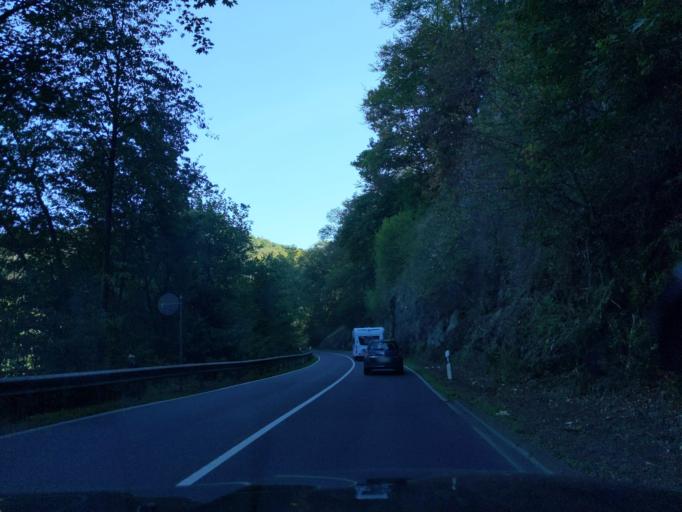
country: DE
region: North Rhine-Westphalia
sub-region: Regierungsbezirk Koln
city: Eitorf
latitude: 50.7611
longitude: 7.3928
